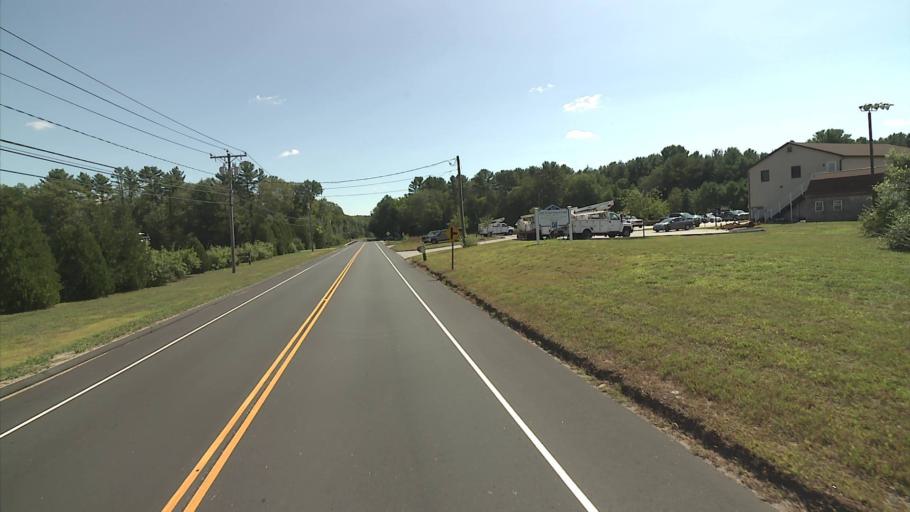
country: US
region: Connecticut
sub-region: New London County
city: Jewett City
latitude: 41.5829
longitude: -71.9123
